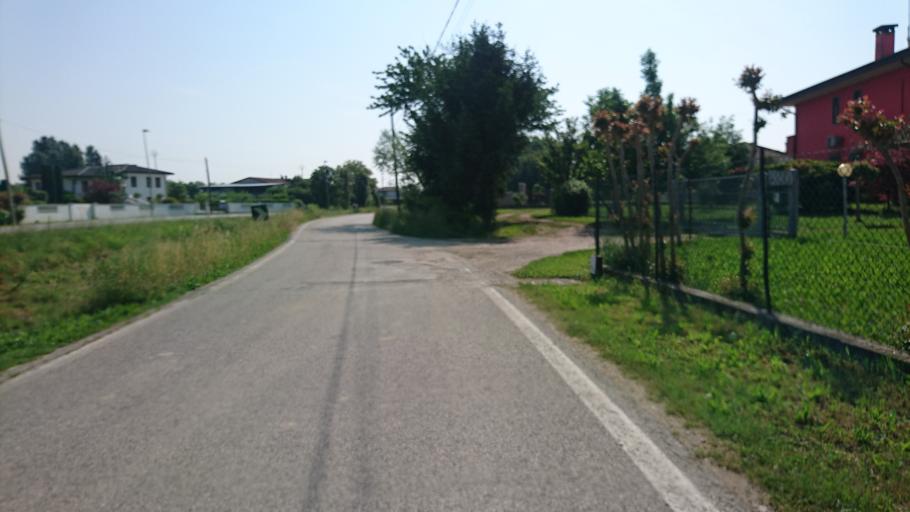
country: IT
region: Veneto
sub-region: Provincia di Venezia
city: Galta
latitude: 45.3677
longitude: 12.0252
